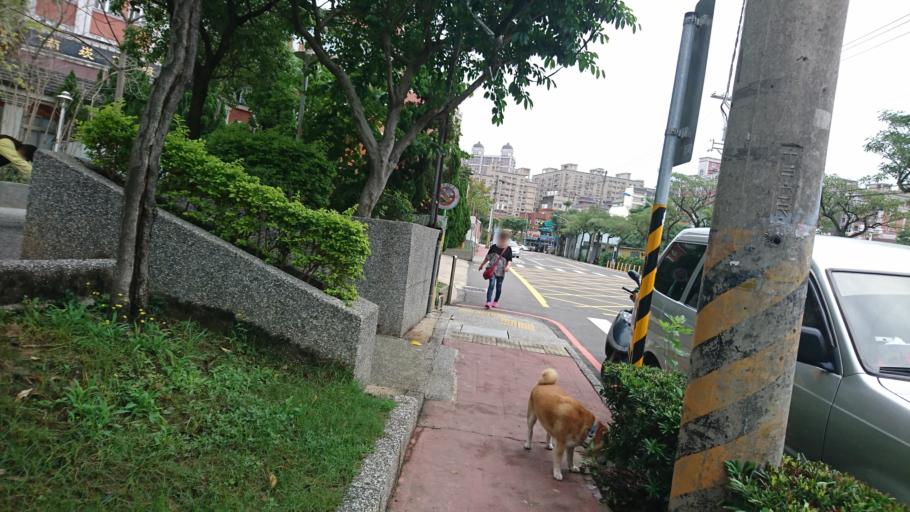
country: TW
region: Taiwan
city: Taoyuan City
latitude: 25.0529
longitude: 121.2964
